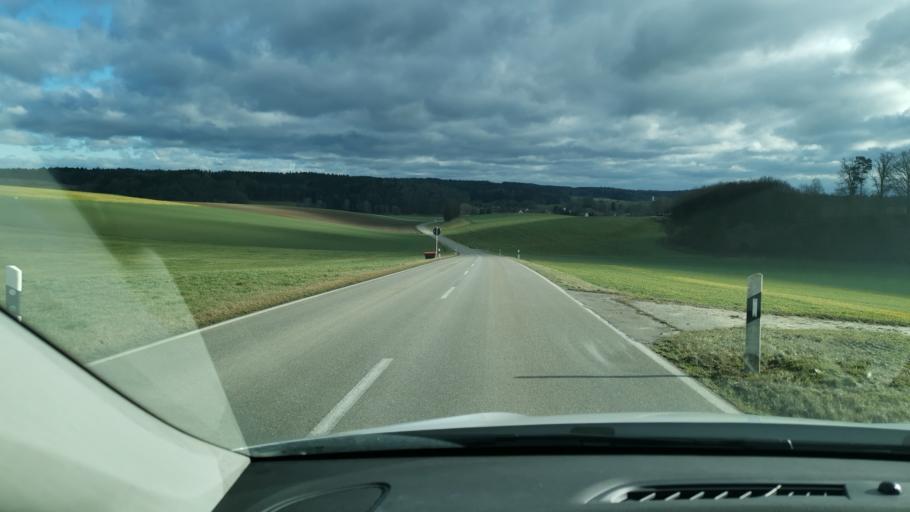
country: DE
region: Bavaria
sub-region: Swabia
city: Aindling
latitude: 48.5588
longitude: 10.9705
